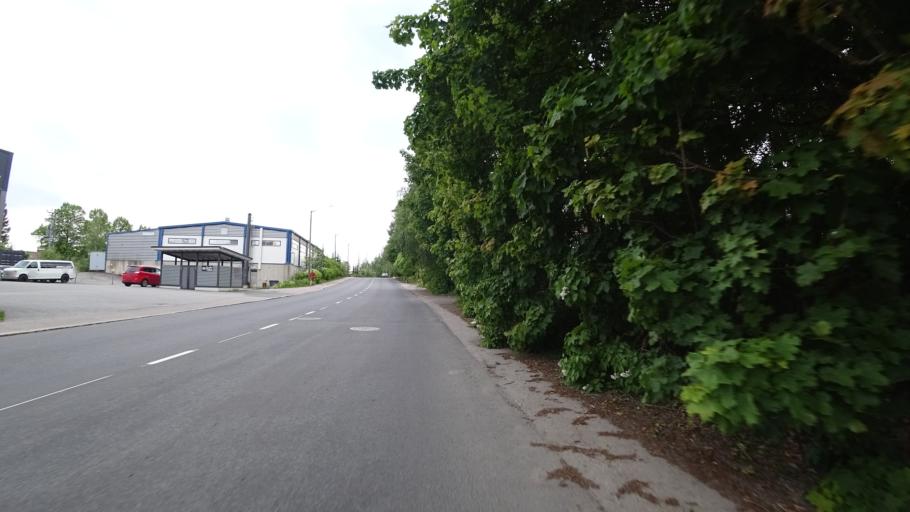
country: FI
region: Pirkanmaa
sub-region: Tampere
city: Pirkkala
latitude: 61.5090
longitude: 23.6666
